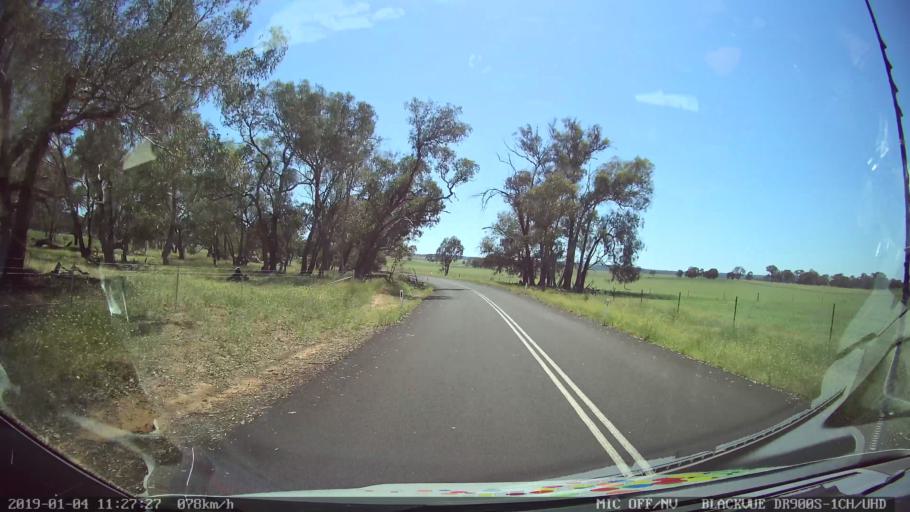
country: AU
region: New South Wales
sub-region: Cabonne
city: Molong
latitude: -33.1090
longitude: 148.7630
